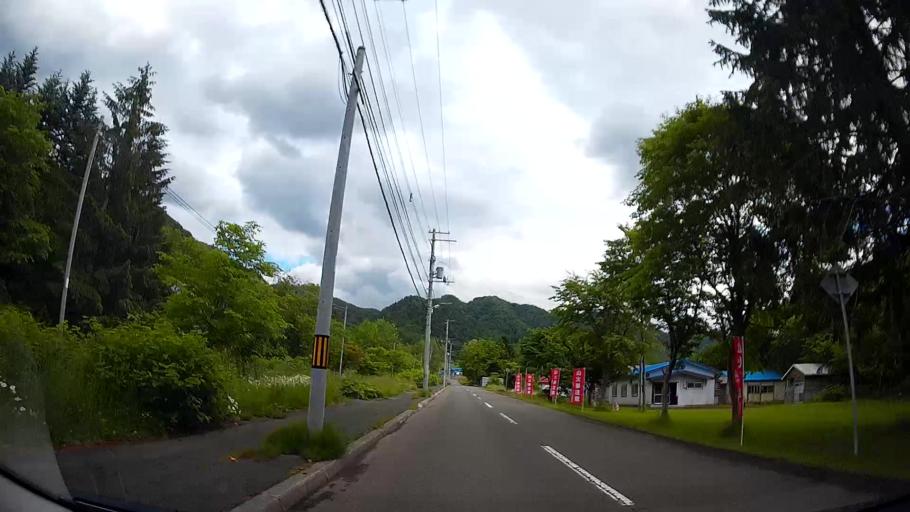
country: JP
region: Hokkaido
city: Sapporo
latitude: 42.9513
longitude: 141.1522
